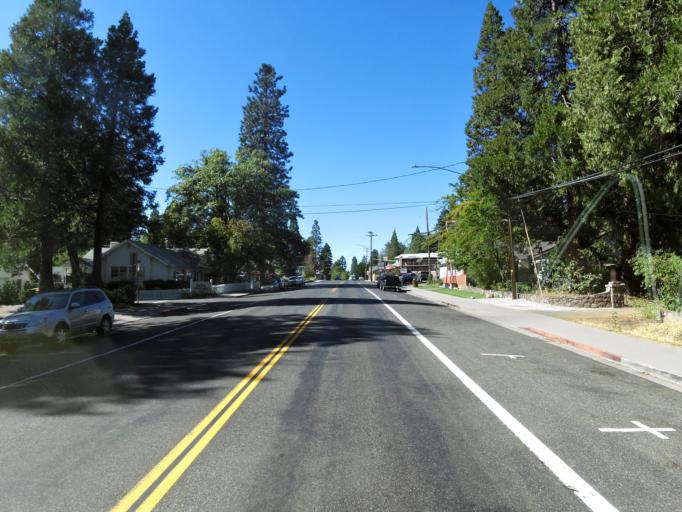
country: US
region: California
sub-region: Siskiyou County
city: Mount Shasta
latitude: 41.3043
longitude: -122.3088
